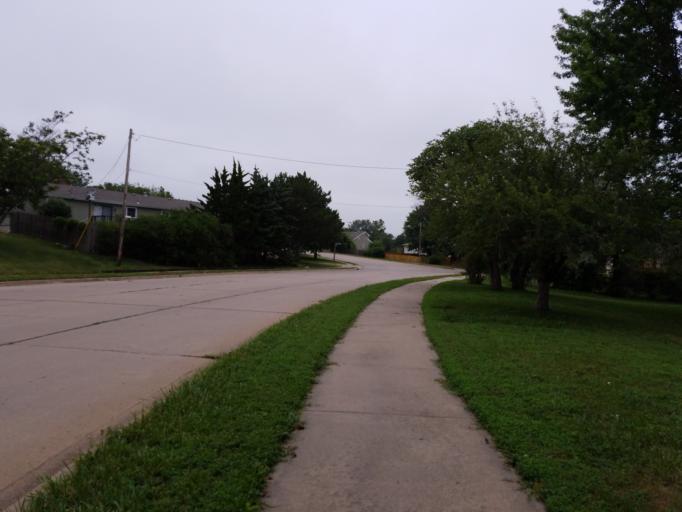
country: US
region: Kansas
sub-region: Riley County
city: Manhattan
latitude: 39.2057
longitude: -96.6246
